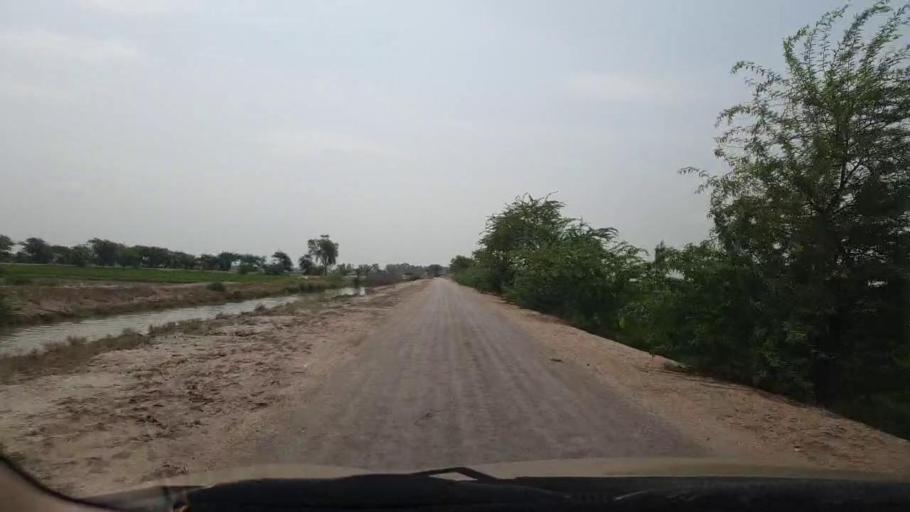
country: PK
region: Sindh
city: Goth Garelo
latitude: 27.5119
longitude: 68.1083
